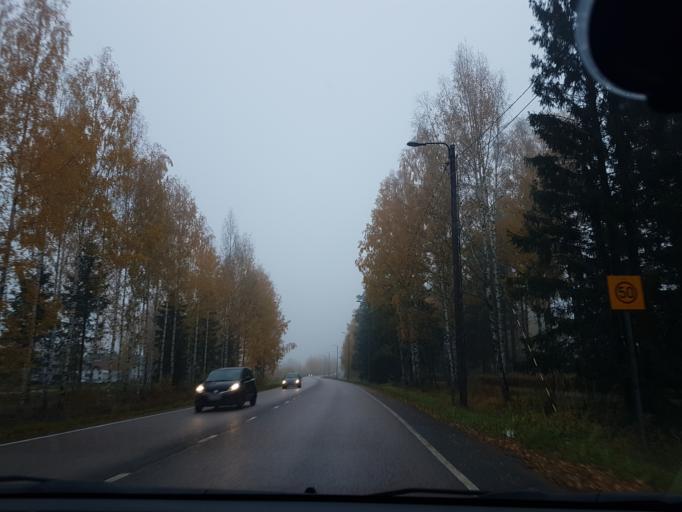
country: FI
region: Uusimaa
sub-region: Helsinki
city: Tuusula
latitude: 60.4050
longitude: 25.0356
